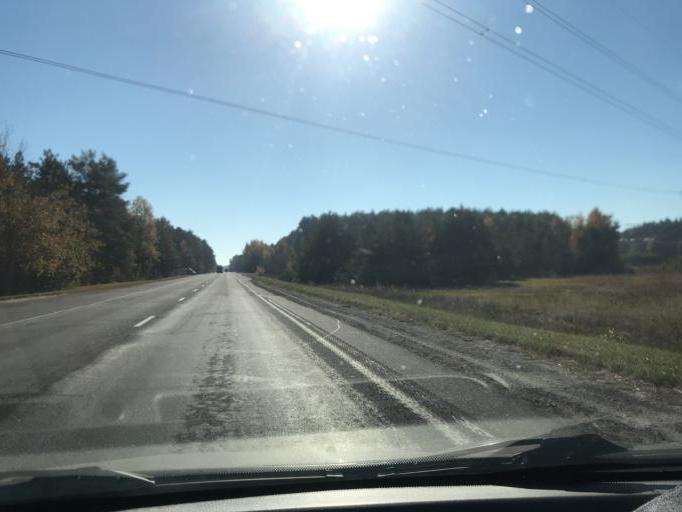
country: BY
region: Gomel
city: Kastsyukowka
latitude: 52.4360
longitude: 30.8263
